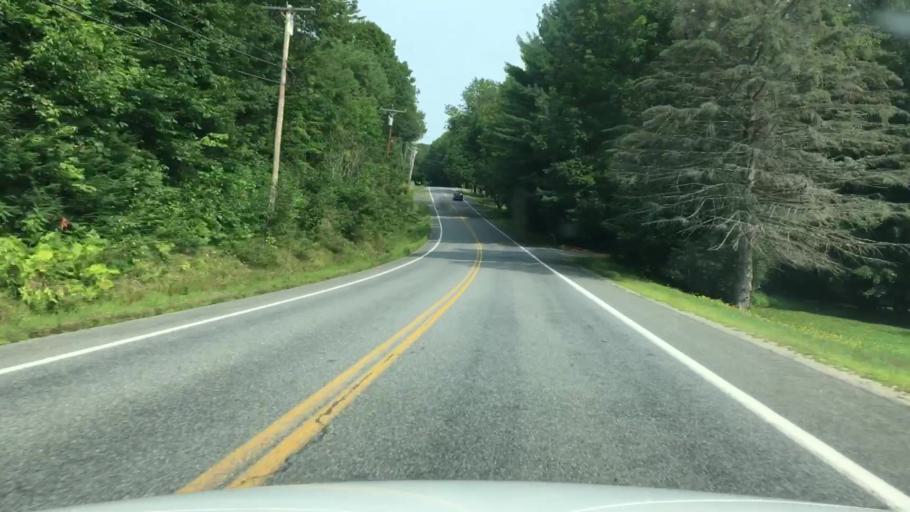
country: US
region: Maine
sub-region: Kennebec County
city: Winthrop
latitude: 44.3167
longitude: -69.9776
